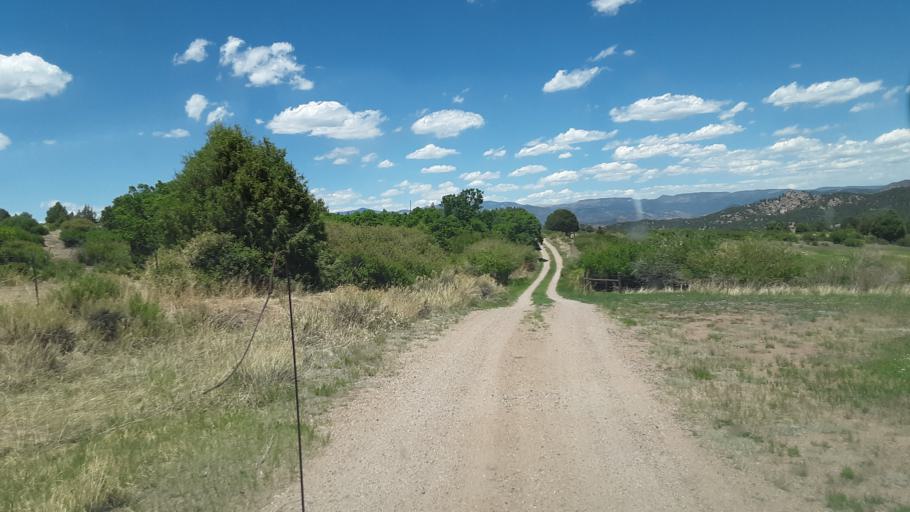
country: US
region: Colorado
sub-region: Custer County
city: Westcliffe
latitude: 38.2815
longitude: -105.6065
